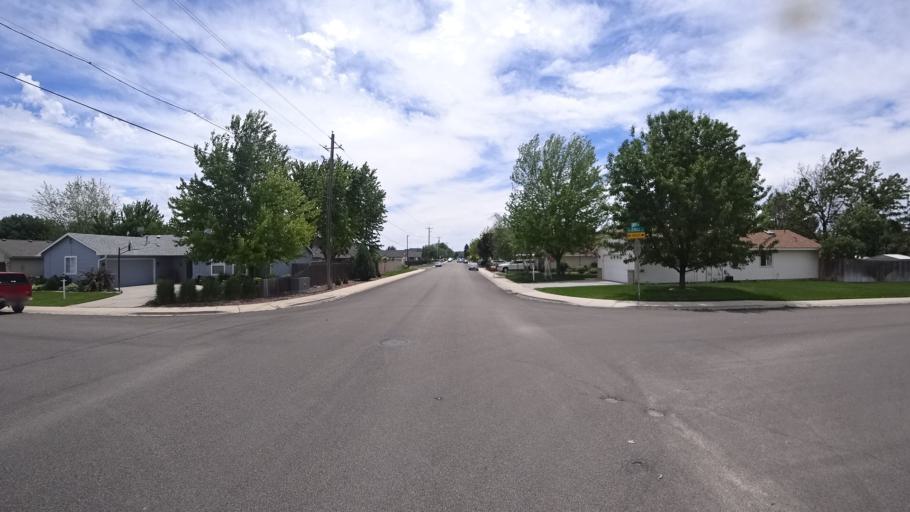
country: US
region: Idaho
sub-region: Ada County
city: Garden City
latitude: 43.6174
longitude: -116.3092
